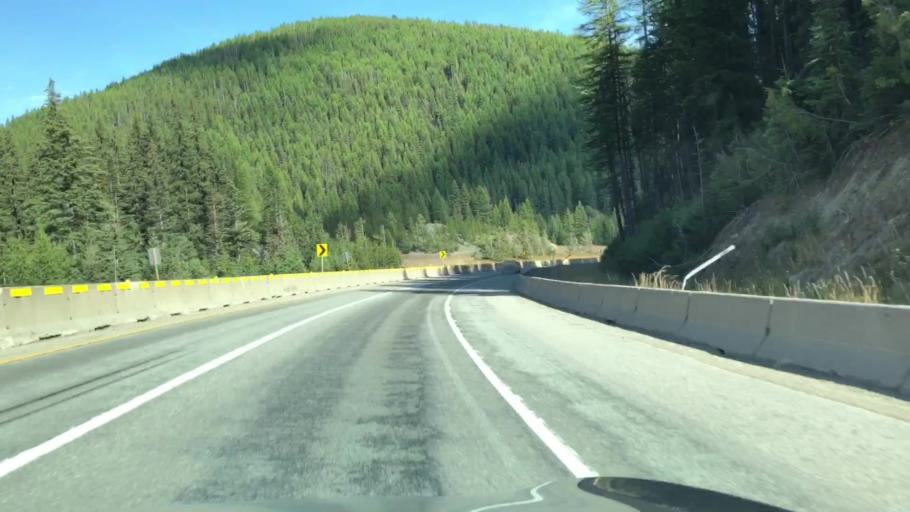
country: US
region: Idaho
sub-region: Shoshone County
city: Wallace
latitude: 47.4360
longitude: -115.6585
